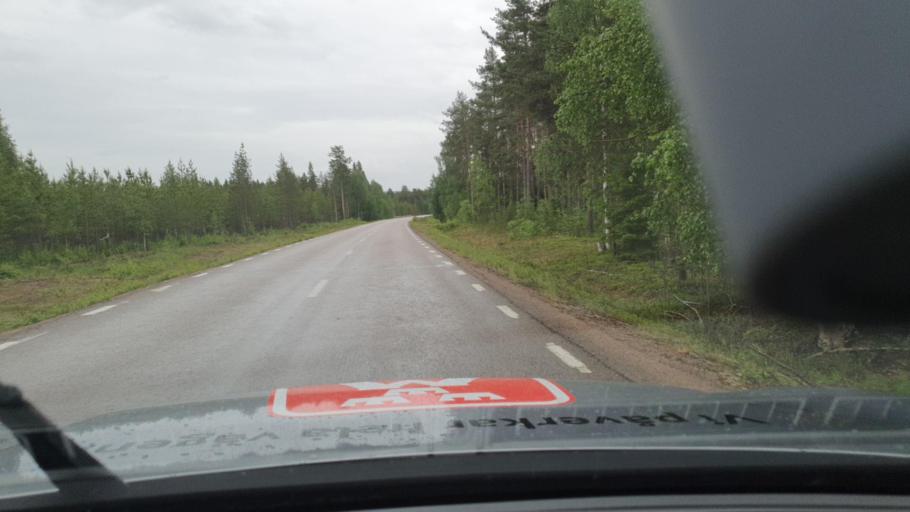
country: SE
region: Norrbotten
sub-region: Overkalix Kommun
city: OEverkalix
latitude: 66.6216
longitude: 22.7451
